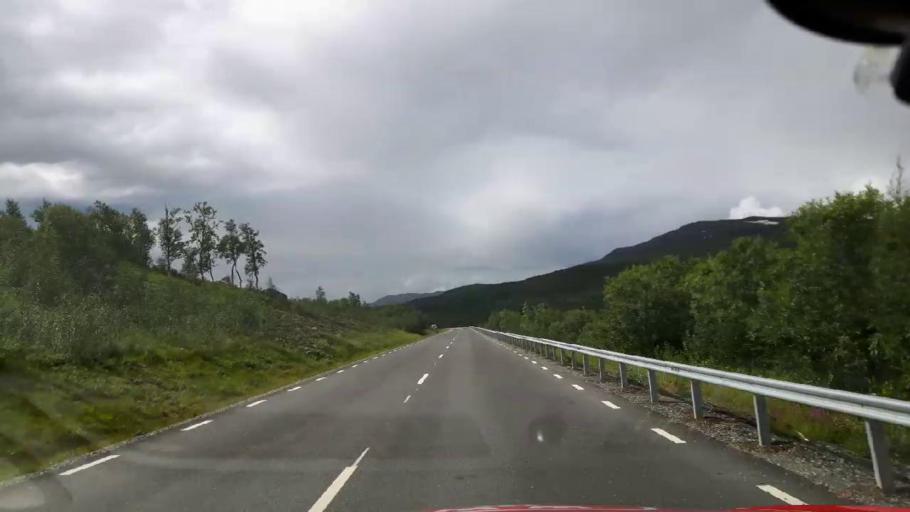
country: NO
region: Nordland
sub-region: Hattfjelldal
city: Hattfjelldal
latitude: 64.9902
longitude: 14.2209
